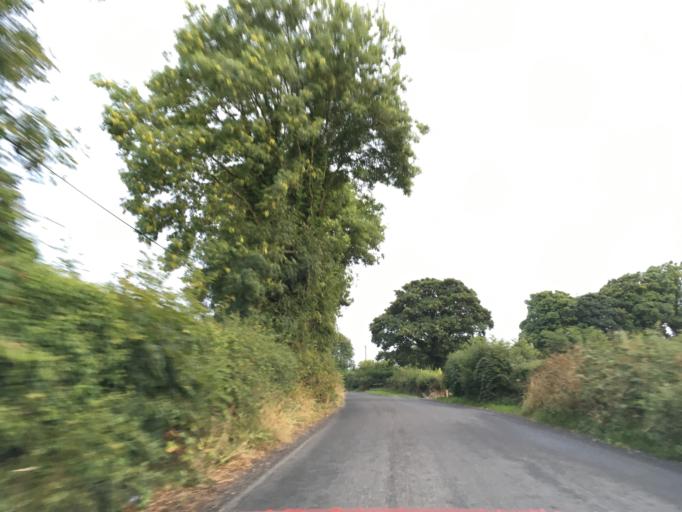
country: IE
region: Munster
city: Cashel
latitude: 52.4732
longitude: -7.9798
